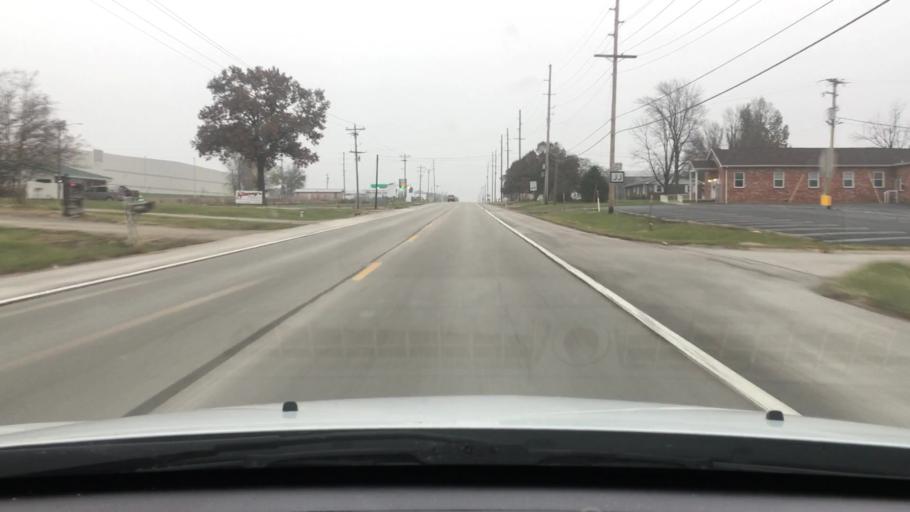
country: US
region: Missouri
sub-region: Audrain County
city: Mexico
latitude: 39.1634
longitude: -91.8342
